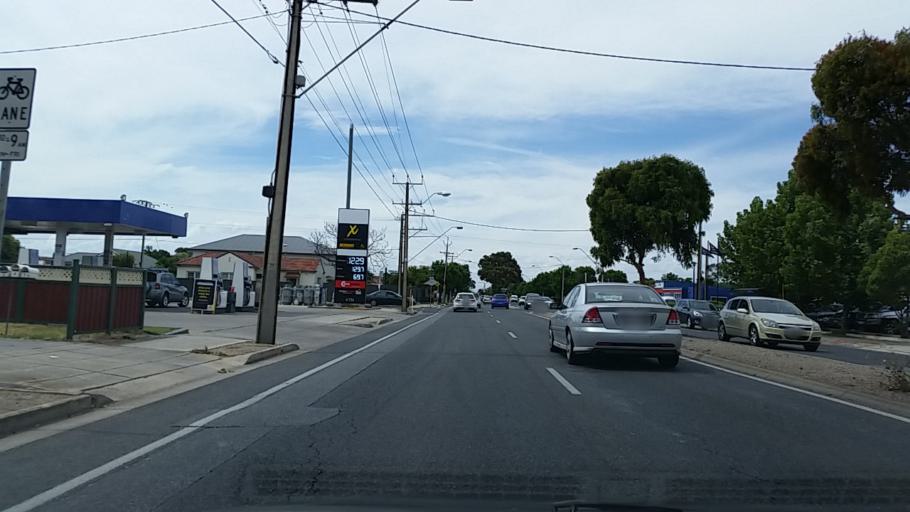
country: AU
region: South Australia
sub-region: City of West Torrens
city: Plympton
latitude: -34.9519
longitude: 138.5539
